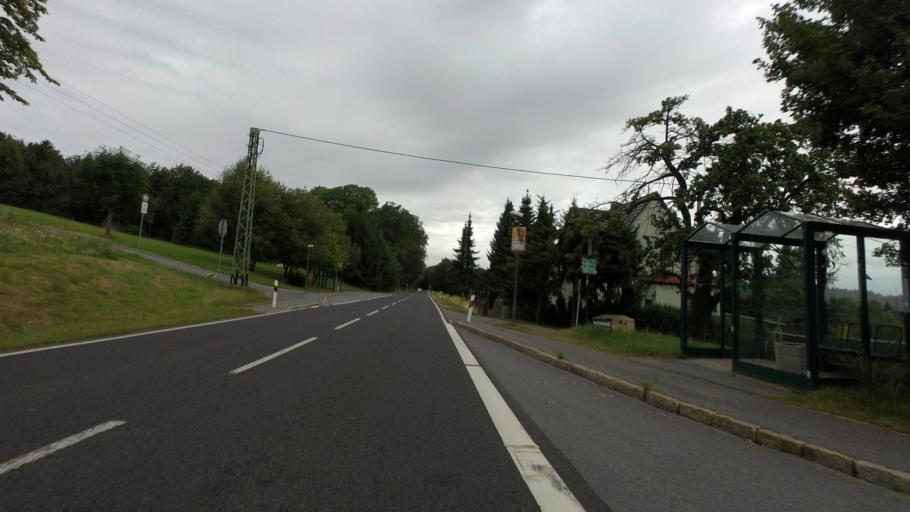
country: DE
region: Saxony
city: Neustadt in Sachsen
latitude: 50.9994
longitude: 14.2439
